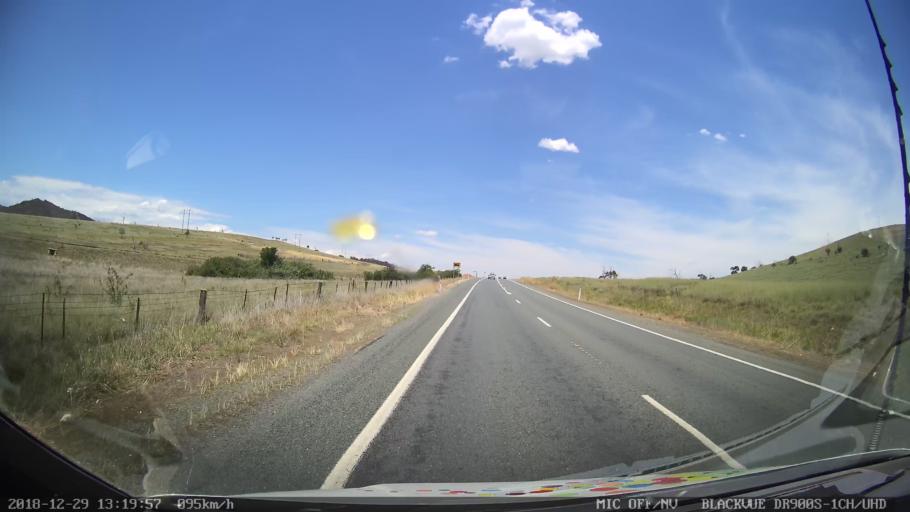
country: AU
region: Australian Capital Territory
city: Macarthur
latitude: -35.7727
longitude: 149.1619
